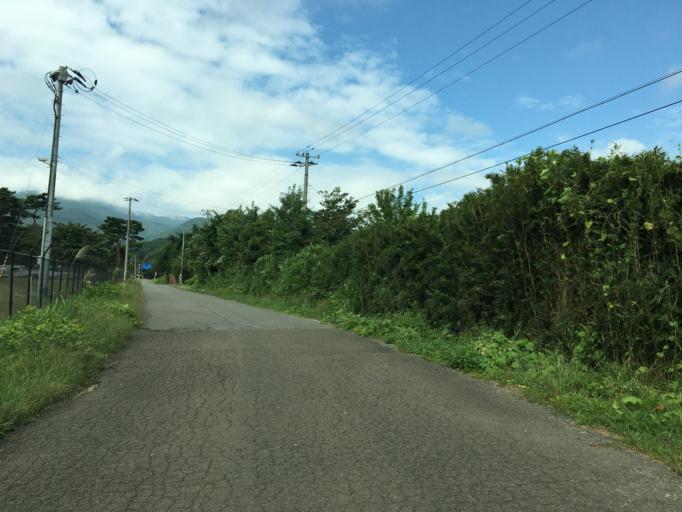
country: JP
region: Fukushima
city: Nihommatsu
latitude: 37.5786
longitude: 140.3551
